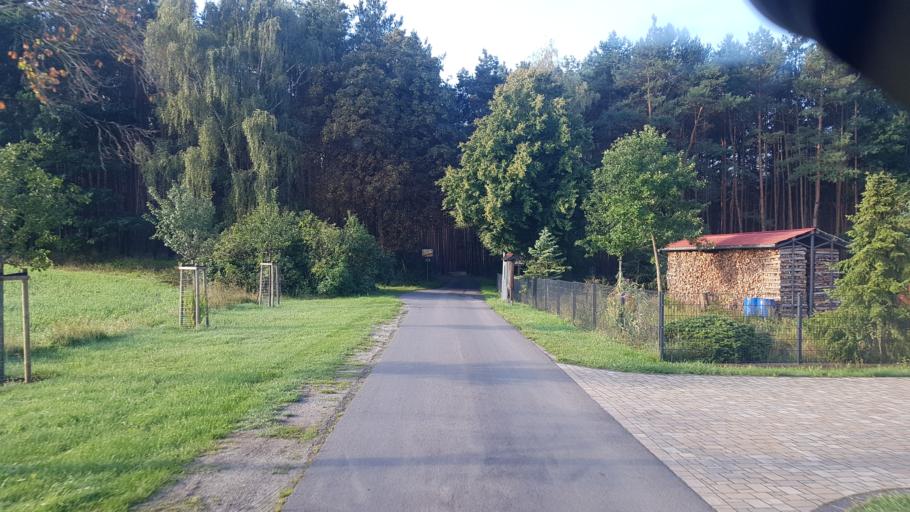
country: DE
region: Brandenburg
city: Bronkow
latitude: 51.6726
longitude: 13.8915
